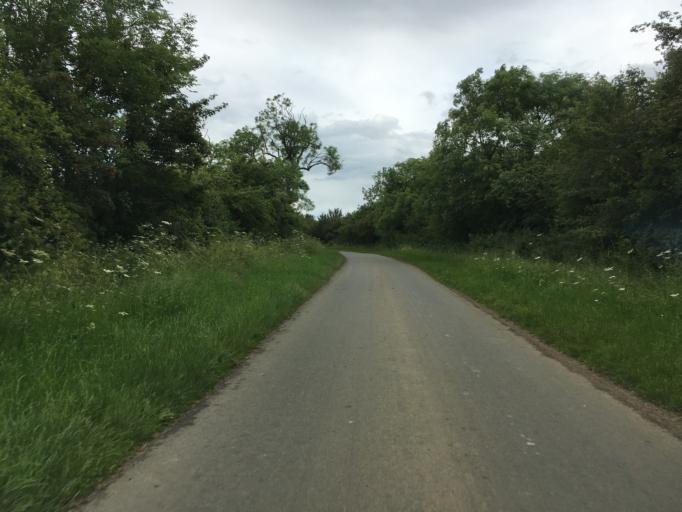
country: GB
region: England
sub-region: Wiltshire
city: Norton
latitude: 51.5967
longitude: -2.1708
